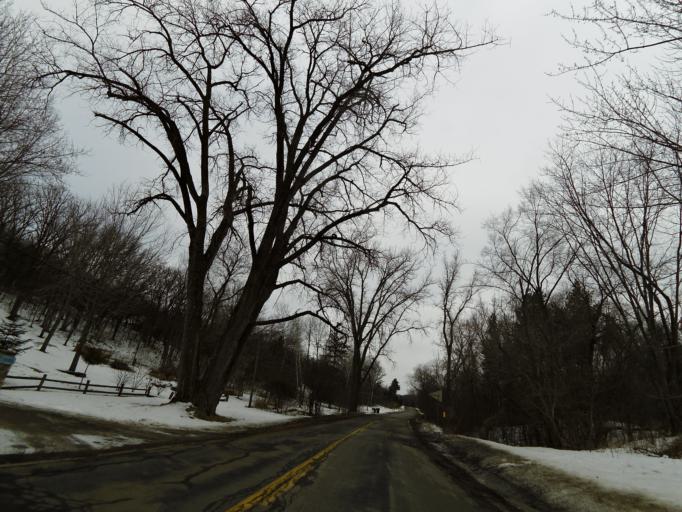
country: US
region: Minnesota
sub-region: Washington County
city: Afton
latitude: 44.8726
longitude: -92.8019
